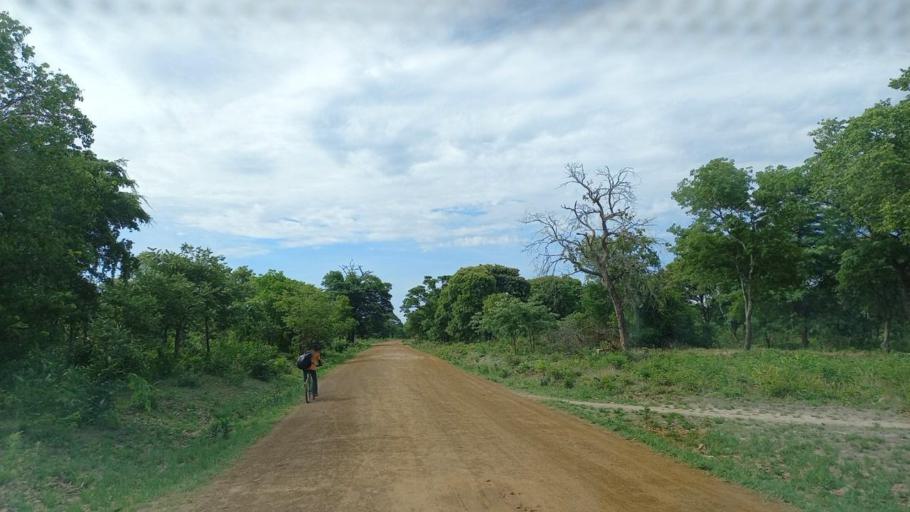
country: ZM
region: North-Western
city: Kabompo
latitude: -13.4567
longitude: 24.4271
